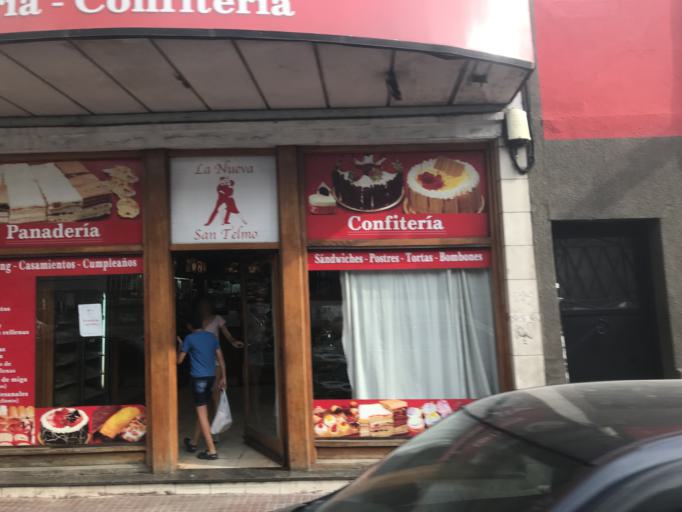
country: AR
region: Buenos Aires F.D.
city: Buenos Aires
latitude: -34.6255
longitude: -58.3737
